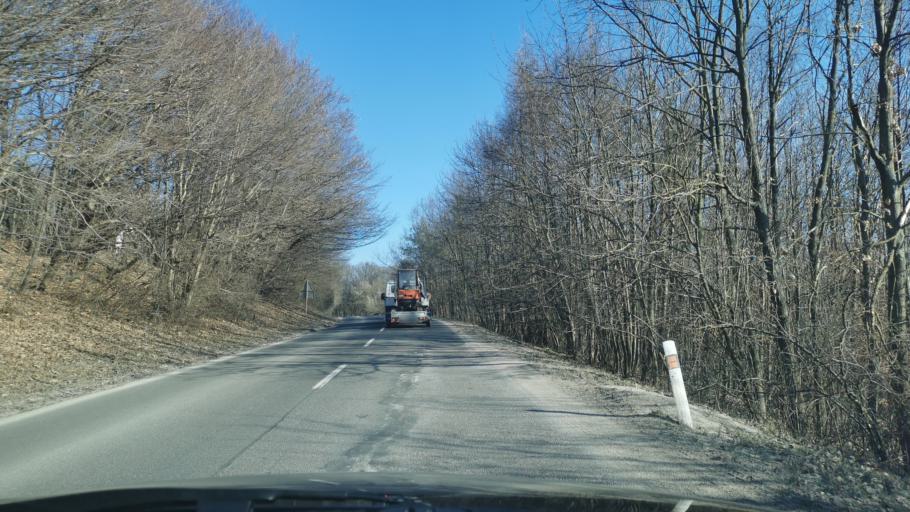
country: SK
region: Trenciansky
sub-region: Okres Myjava
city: Myjava
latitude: 48.7460
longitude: 17.4812
